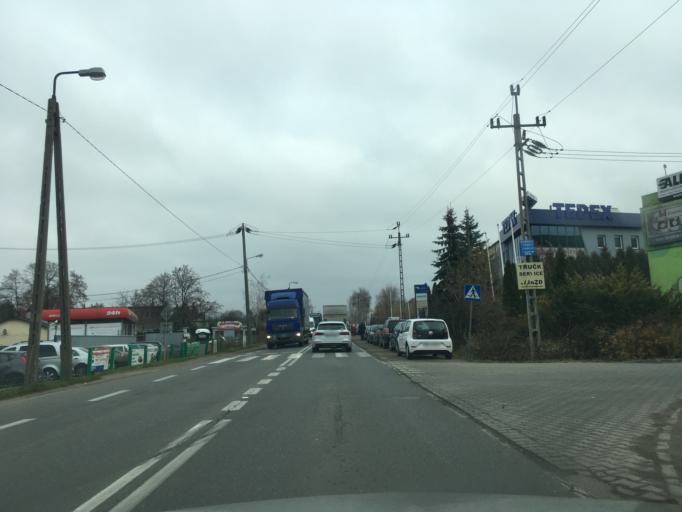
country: PL
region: Masovian Voivodeship
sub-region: Powiat piaseczynski
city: Piaseczno
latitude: 52.0827
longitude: 21.0038
